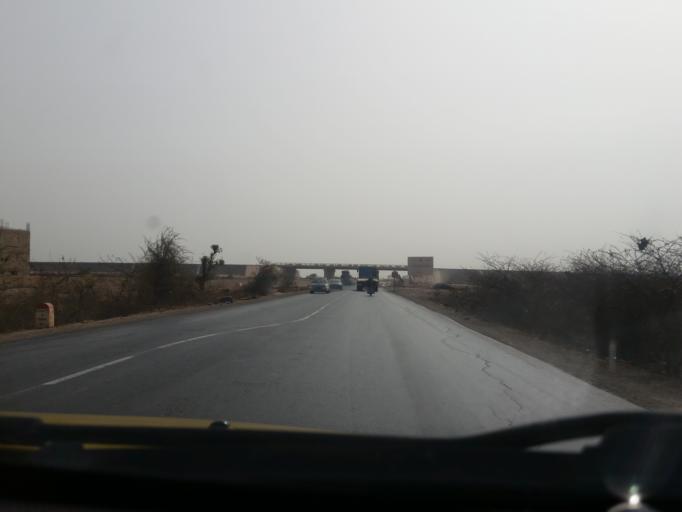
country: SN
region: Thies
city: Pout
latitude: 14.7295
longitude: -17.1627
